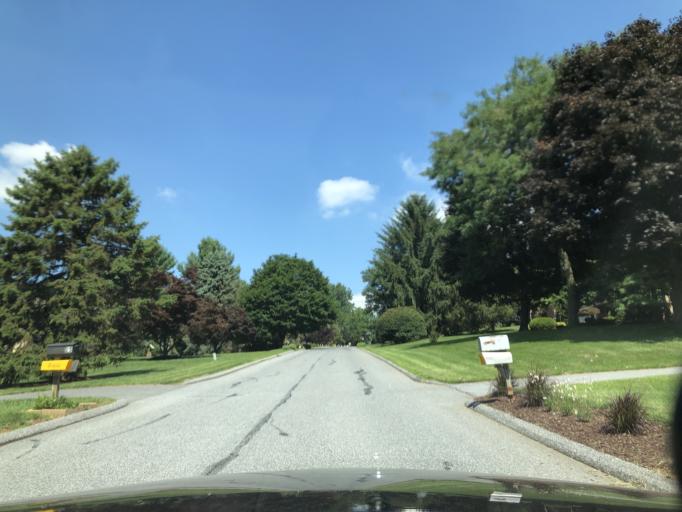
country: US
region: Maryland
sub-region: Carroll County
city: Westminster
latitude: 39.6194
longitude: -77.0003
